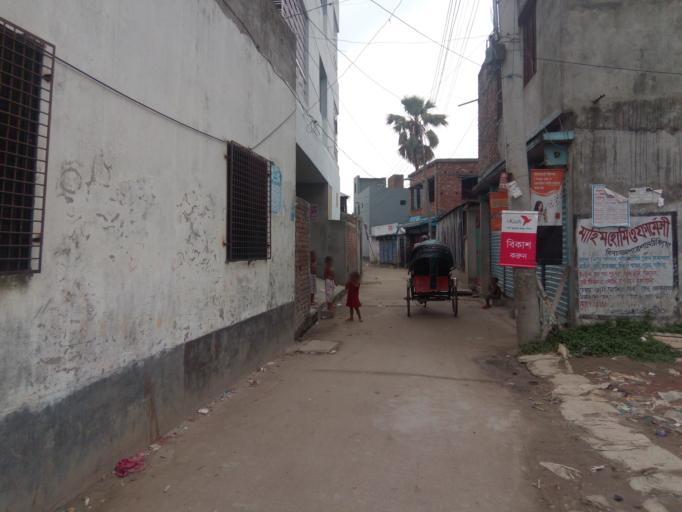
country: BD
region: Dhaka
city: Paltan
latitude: 23.7541
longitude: 90.4368
